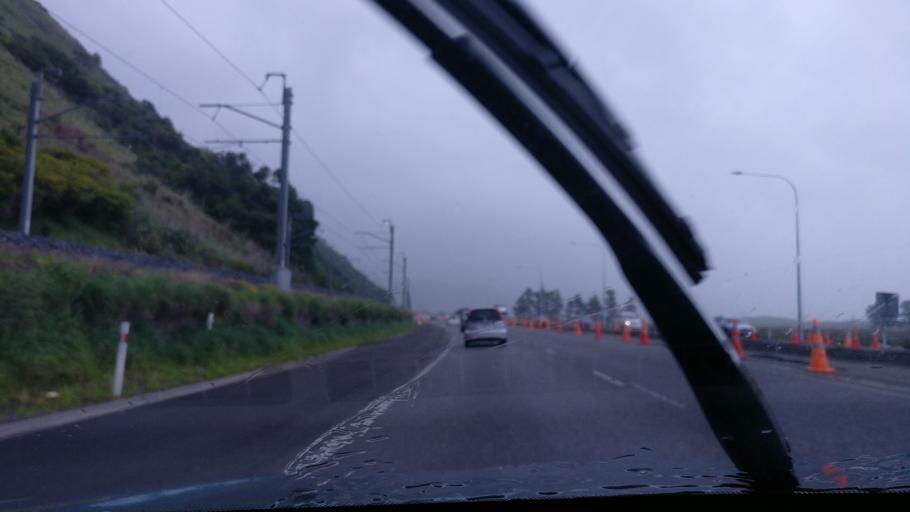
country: NZ
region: Wellington
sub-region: Kapiti Coast District
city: Paraparaumu
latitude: -40.9437
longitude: 174.9918
